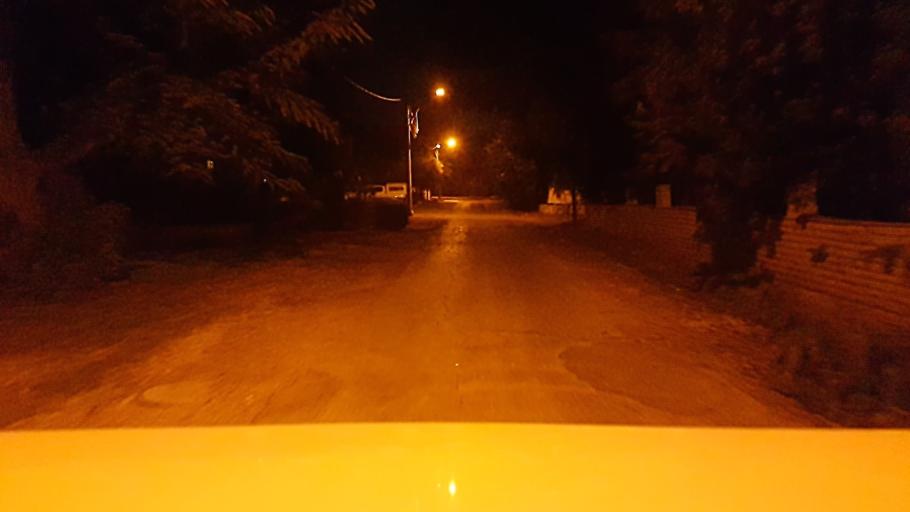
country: IL
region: Central District
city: Nehalim
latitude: 32.0766
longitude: 34.9209
